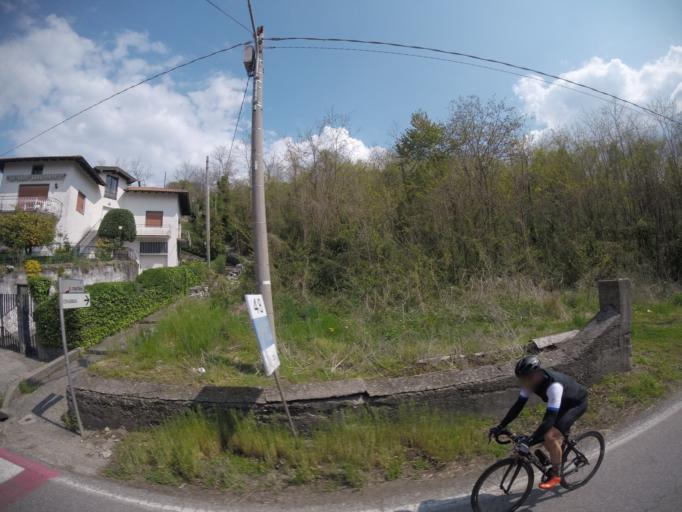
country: IT
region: Piedmont
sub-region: Provincia di Novara
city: Pettenasco
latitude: 45.8270
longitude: 8.3991
